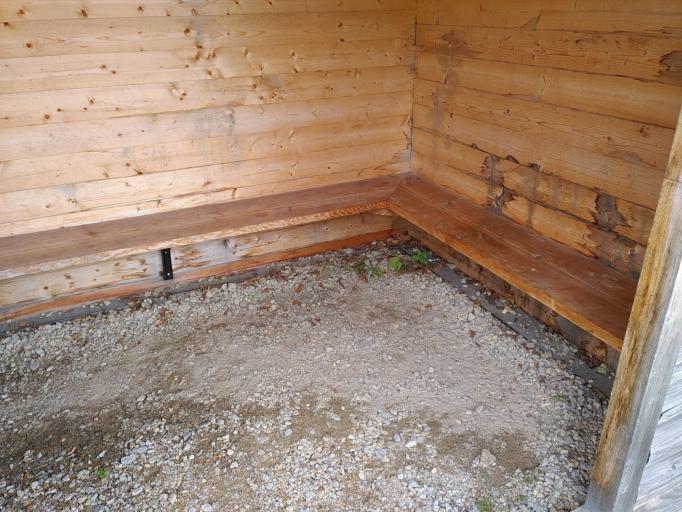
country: DE
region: Bavaria
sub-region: Lower Bavaria
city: Frauenau
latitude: 49.0603
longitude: 13.3341
